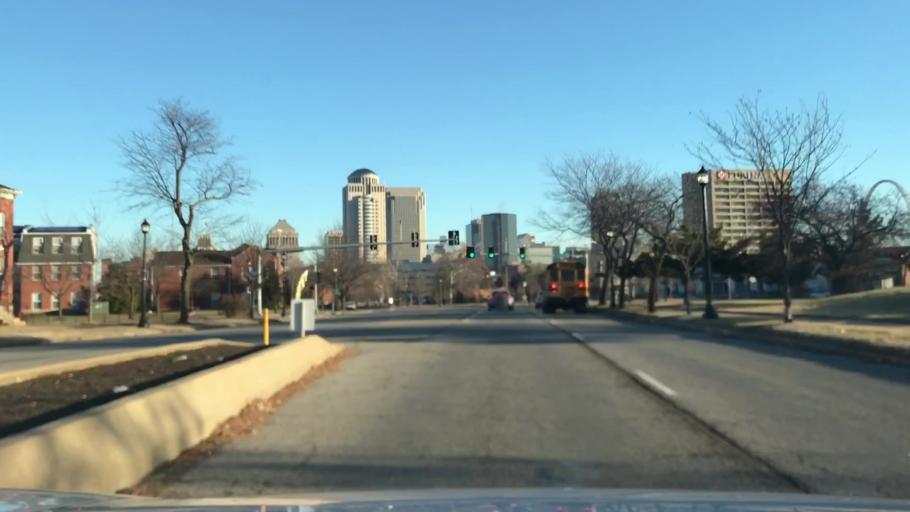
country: US
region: Missouri
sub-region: City of Saint Louis
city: St. Louis
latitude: 38.6160
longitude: -90.2031
